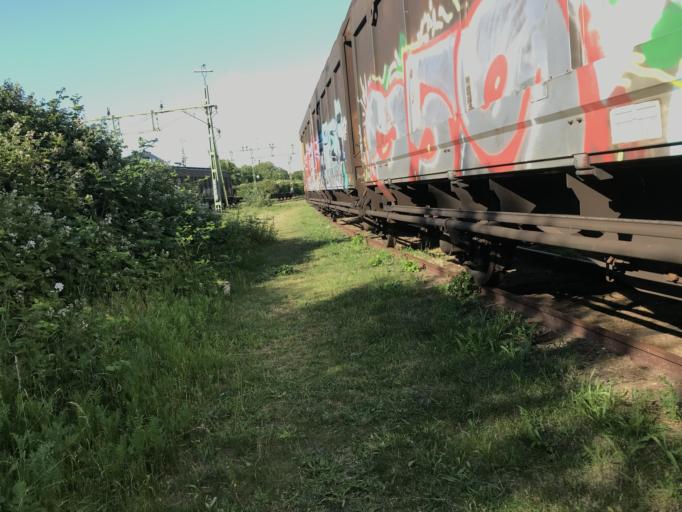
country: SE
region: Skane
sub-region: Landskrona
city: Landskrona
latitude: 55.8658
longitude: 12.8288
